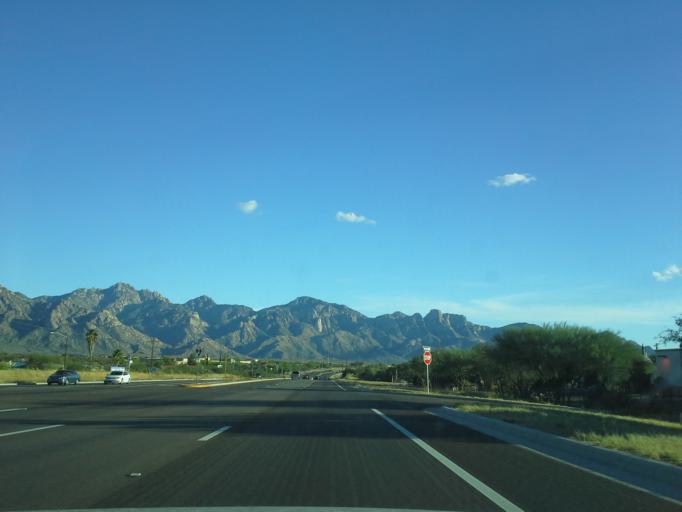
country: US
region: Arizona
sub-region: Pima County
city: Catalina
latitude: 32.4905
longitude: -110.9248
